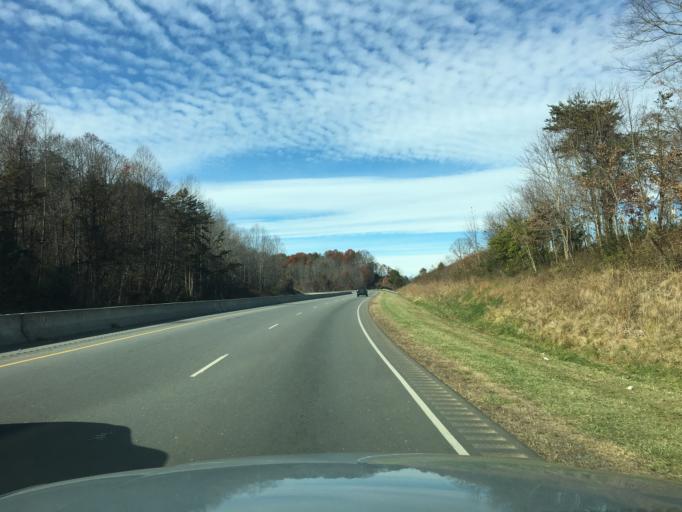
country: US
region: North Carolina
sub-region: McDowell County
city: Marion
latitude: 35.6643
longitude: -81.9802
